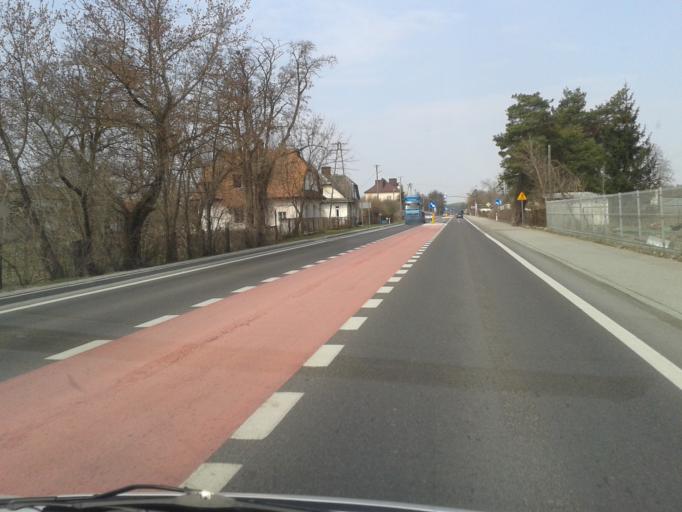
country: PL
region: Lublin Voivodeship
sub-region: Powiat tomaszowski
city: Belzec
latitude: 50.3740
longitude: 23.4527
